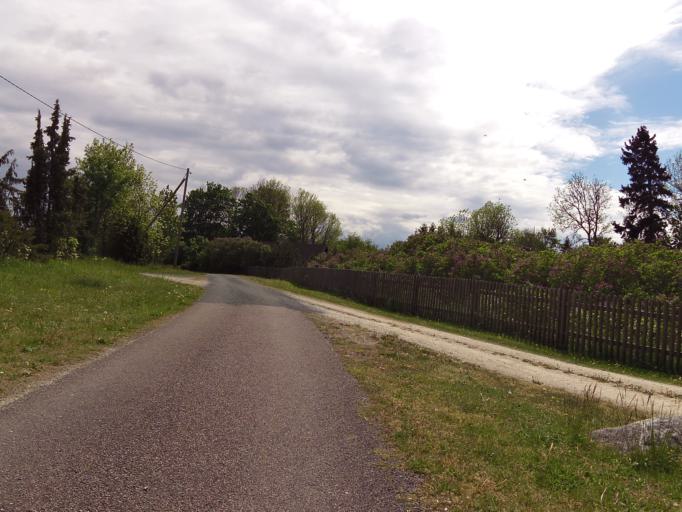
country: EE
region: Harju
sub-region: Paldiski linn
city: Paldiski
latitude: 59.2569
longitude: 23.7462
